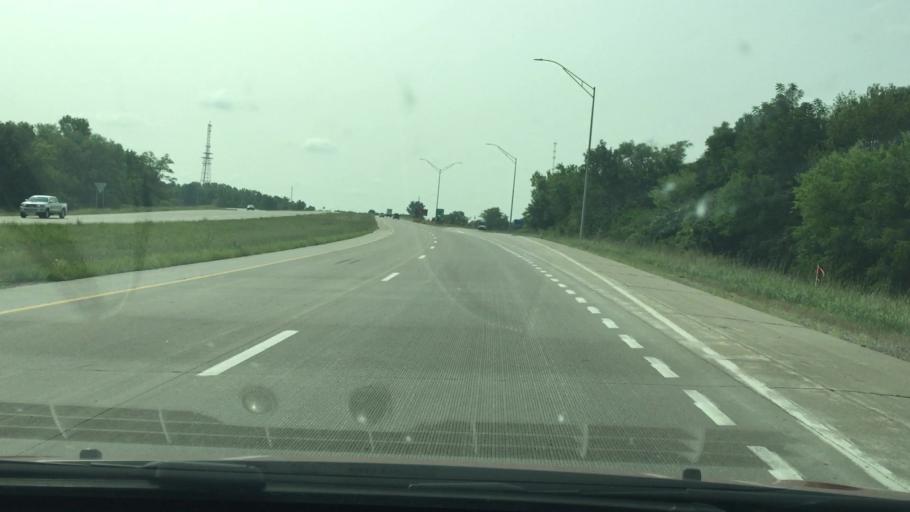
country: US
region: Iowa
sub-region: Scott County
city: Buffalo
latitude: 41.5142
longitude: -90.6746
